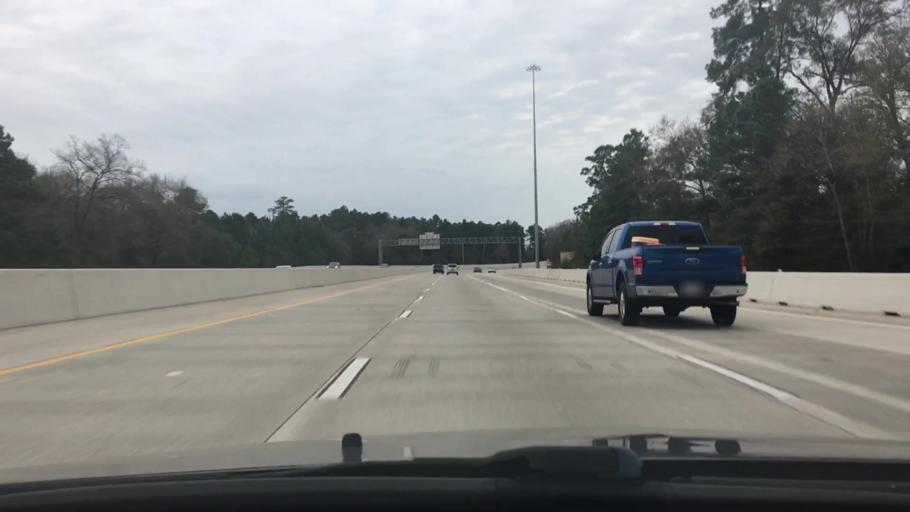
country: US
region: Texas
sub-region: Harris County
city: Spring
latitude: 30.0813
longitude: -95.4113
